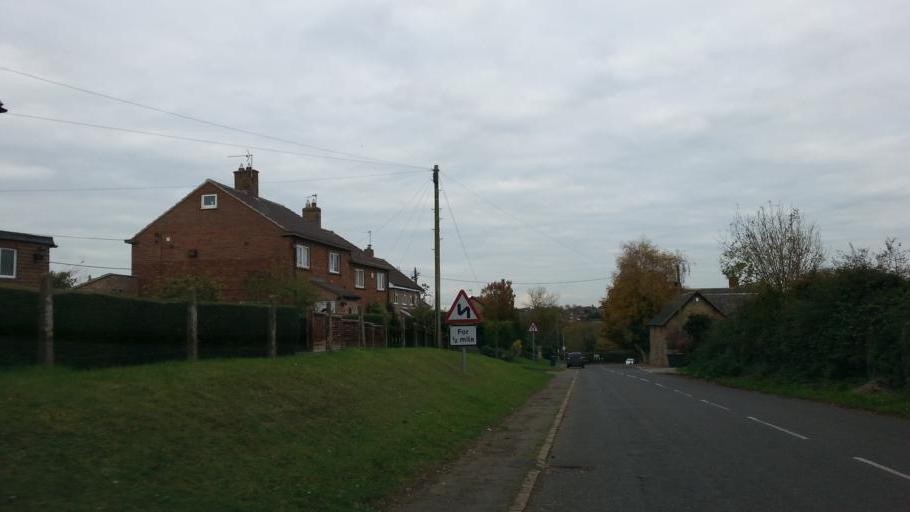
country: GB
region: England
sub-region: Northamptonshire
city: Desborough
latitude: 52.4812
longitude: -0.8151
